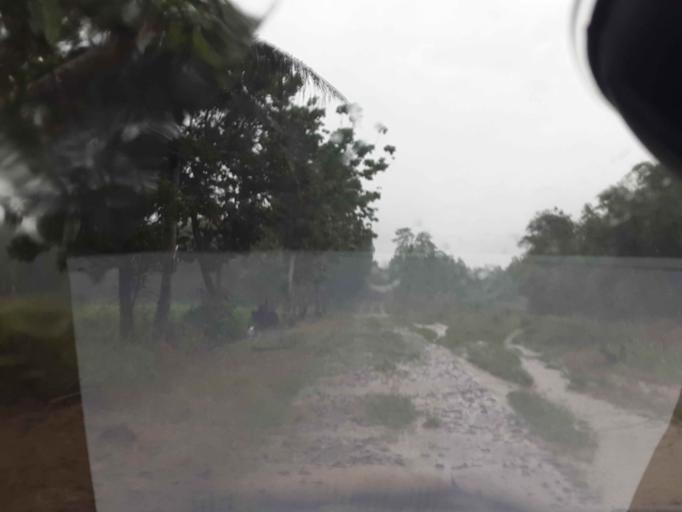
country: ID
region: Lampung
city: Kedaton
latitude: -5.3921
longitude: 105.3386
